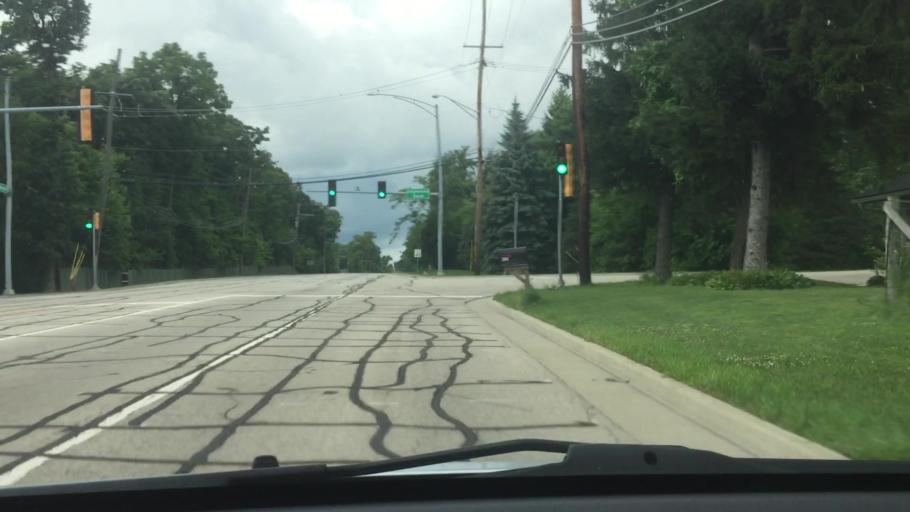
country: US
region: Illinois
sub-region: McHenry County
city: Crystal Lake
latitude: 42.2841
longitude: -88.3208
